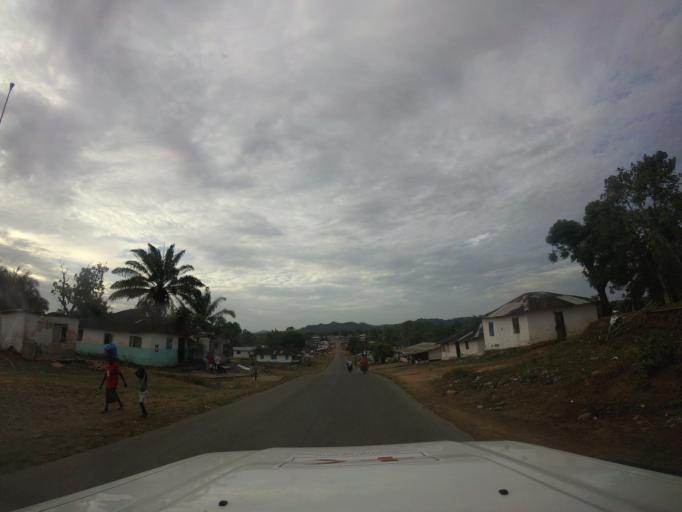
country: LR
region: Bomi
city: Tubmanburg
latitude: 6.8653
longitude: -10.8187
